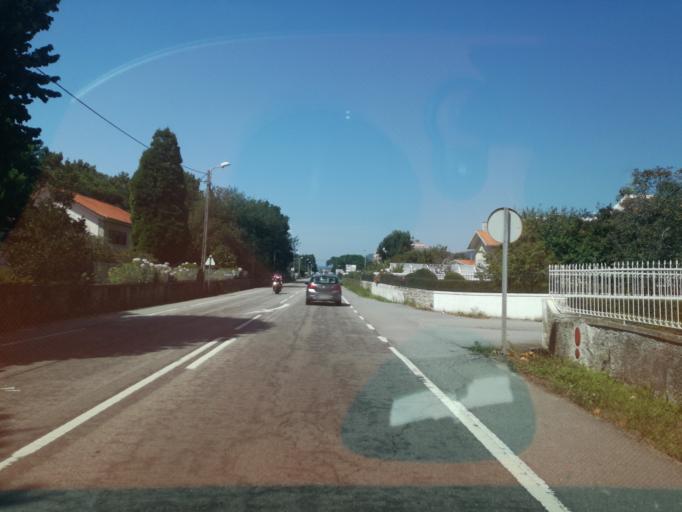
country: PT
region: Braga
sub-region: Esposende
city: Esposende
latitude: 41.5410
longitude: -8.7820
